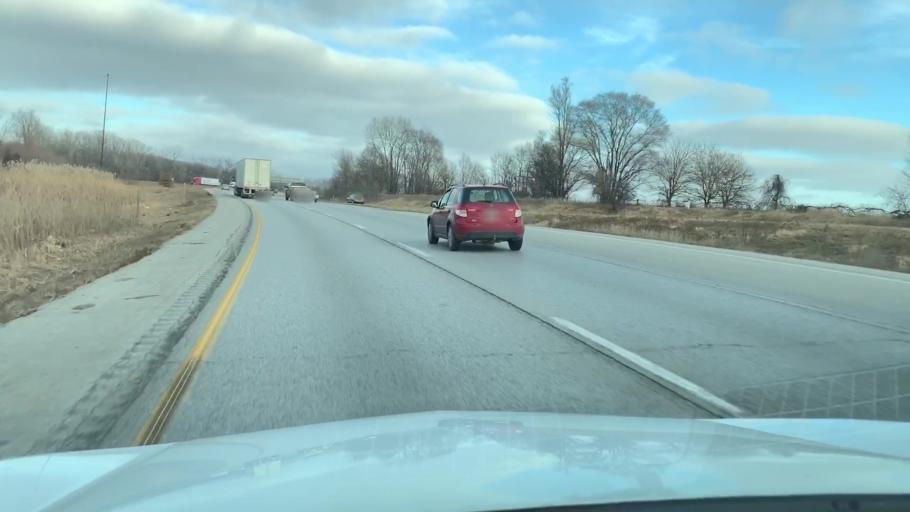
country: US
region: Iowa
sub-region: Polk County
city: Des Moines
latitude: 41.6514
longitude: -93.5733
